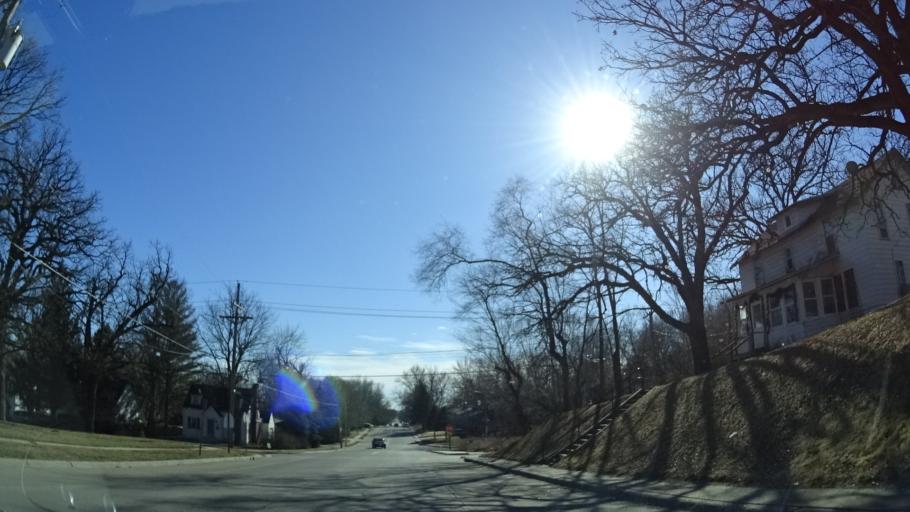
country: US
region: Nebraska
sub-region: Sarpy County
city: Bellevue
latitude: 41.1442
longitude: -95.8937
